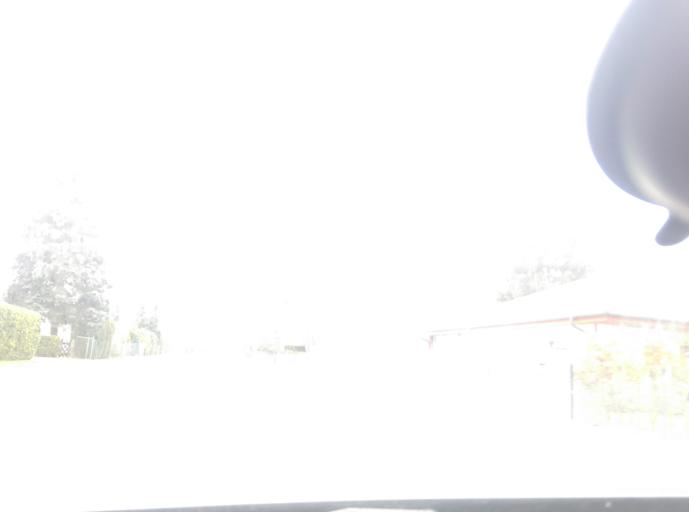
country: DE
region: Lower Saxony
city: Lindwedel
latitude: 52.6159
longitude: 9.6884
